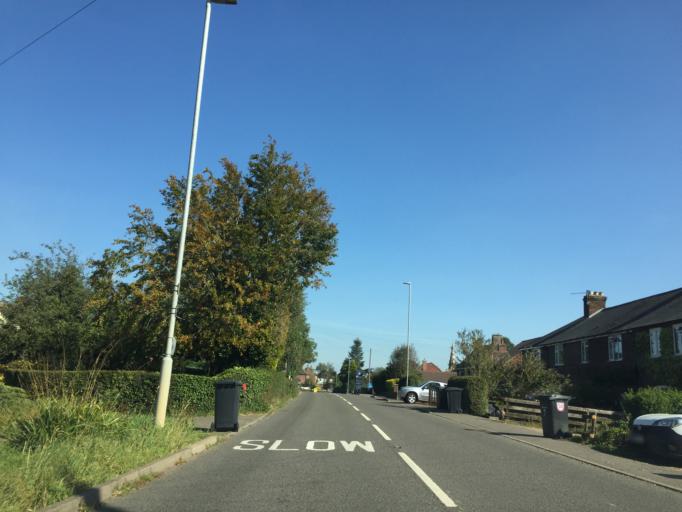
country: GB
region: England
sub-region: Leicestershire
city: Houghton on the Hill
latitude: 52.6436
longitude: -0.9077
